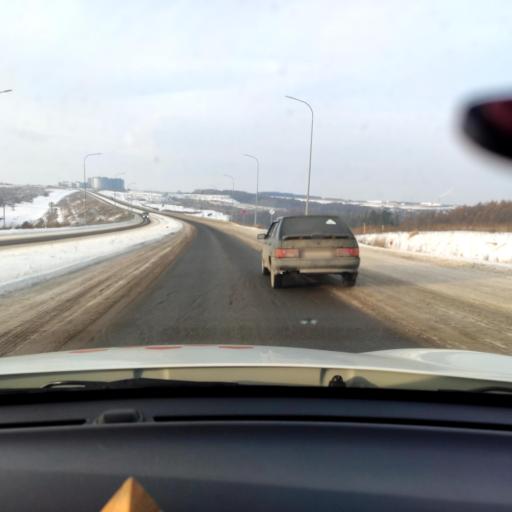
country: RU
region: Tatarstan
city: Sviyazhsk
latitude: 55.7433
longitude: 48.7738
